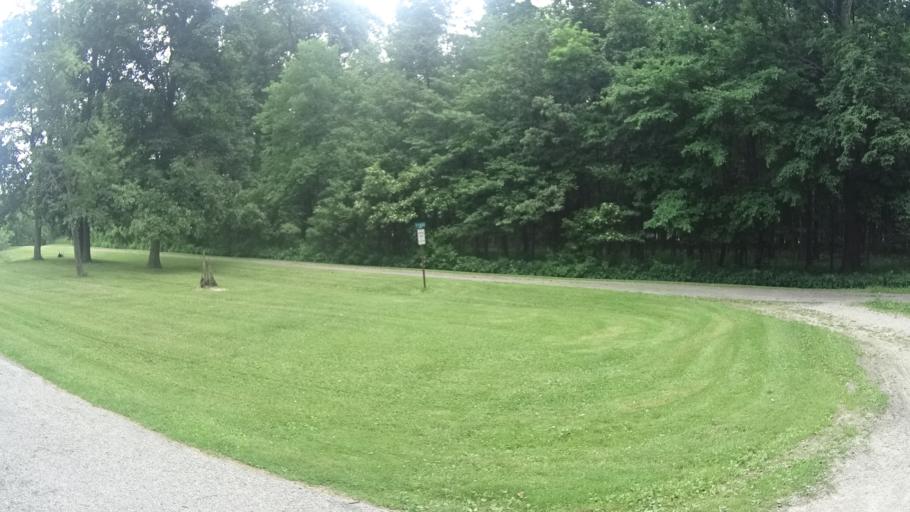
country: US
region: Ohio
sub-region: Huron County
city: Monroeville
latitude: 41.3031
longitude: -82.6722
